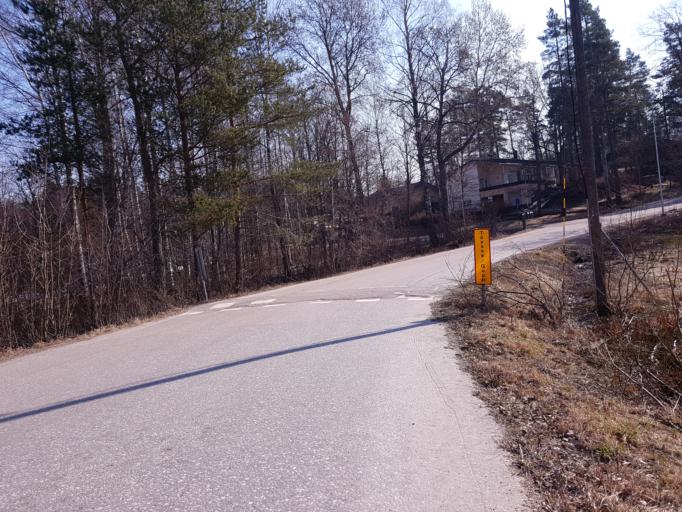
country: FI
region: Uusimaa
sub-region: Helsinki
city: Kilo
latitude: 60.2604
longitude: 24.7776
